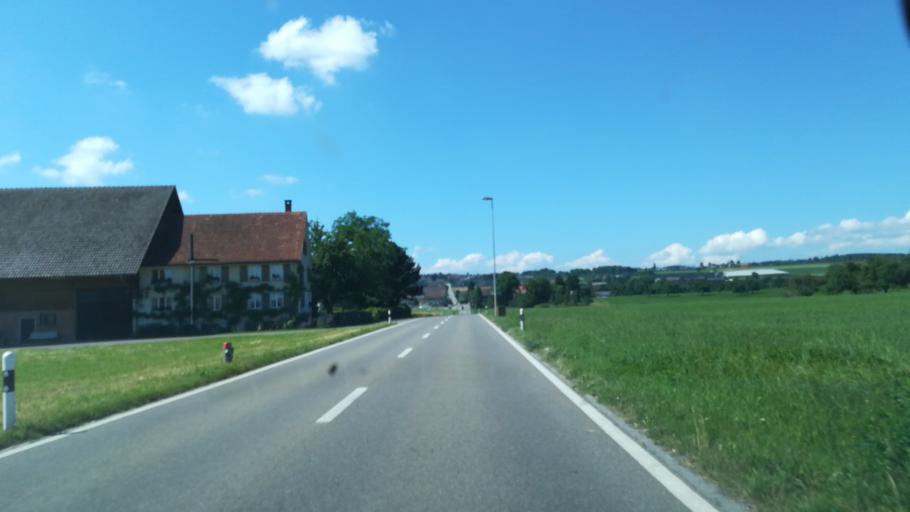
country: CH
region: Thurgau
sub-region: Weinfelden District
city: Sulgen
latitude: 47.5552
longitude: 9.1756
